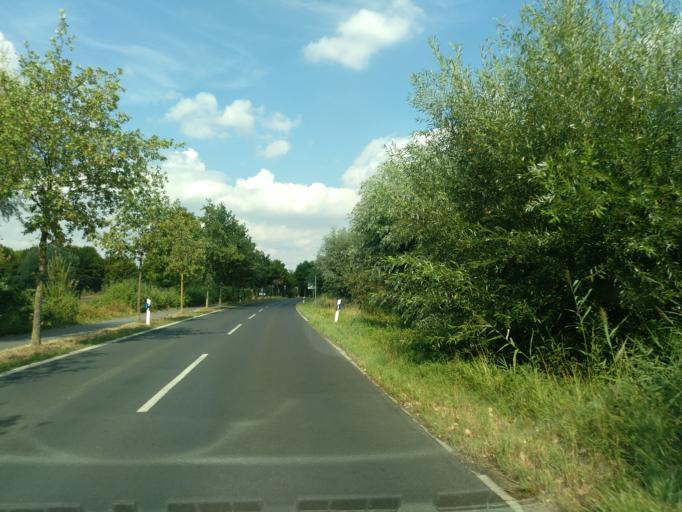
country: DE
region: North Rhine-Westphalia
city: Tonisvorst
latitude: 51.3719
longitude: 6.5259
